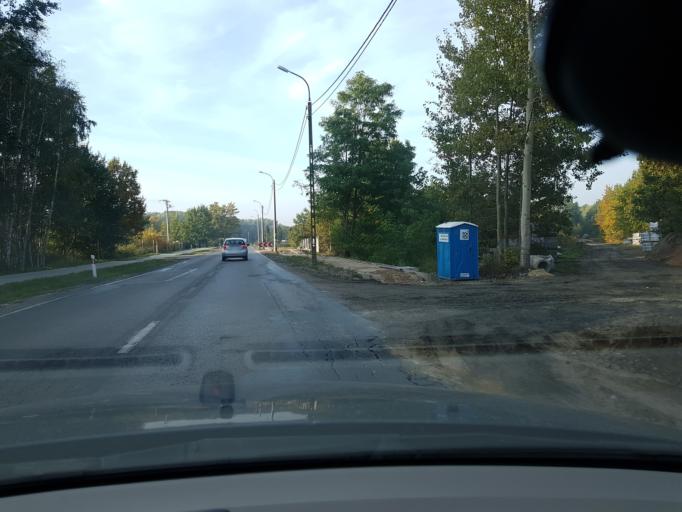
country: PL
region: Masovian Voivodeship
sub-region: Powiat minski
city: Halinow
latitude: 52.1801
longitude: 21.2986
